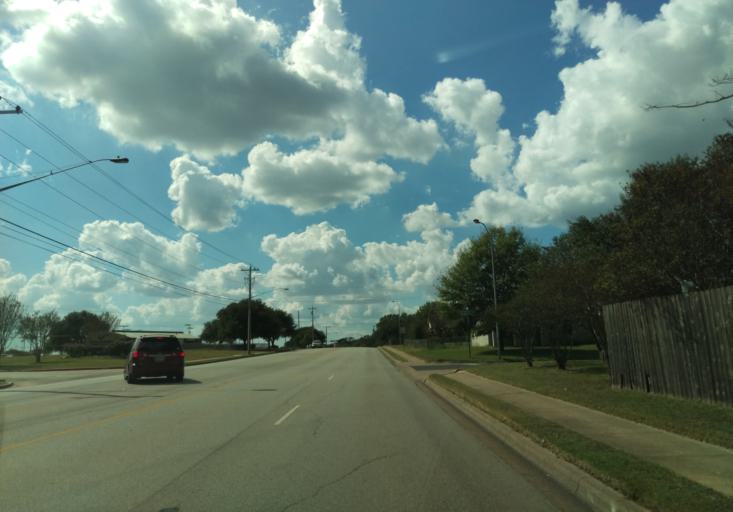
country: US
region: Texas
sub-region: Brazos County
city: College Station
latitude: 30.5813
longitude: -96.2945
